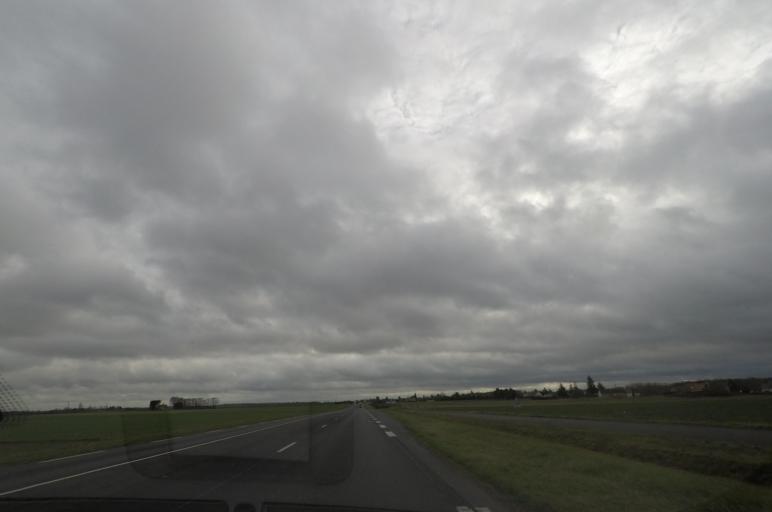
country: FR
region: Centre
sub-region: Departement du Loir-et-Cher
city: Saint-Sulpice-de-Pommeray
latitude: 47.6636
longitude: 1.2550
